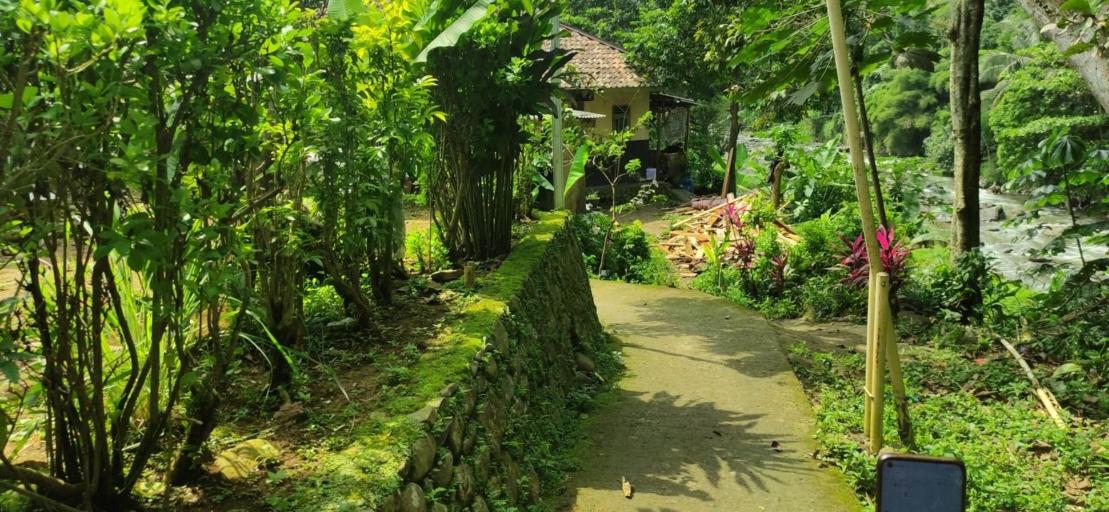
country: ID
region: West Java
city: Caringin
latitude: -6.6471
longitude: 106.8866
